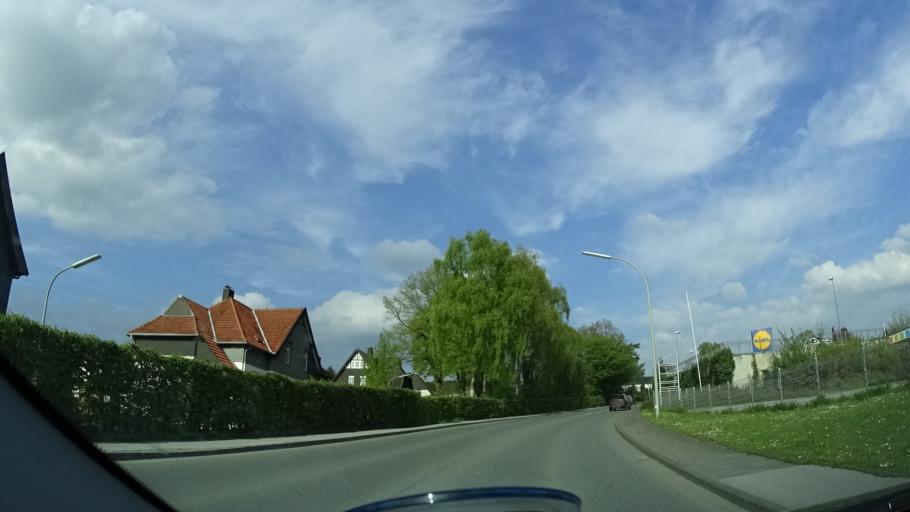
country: DE
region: North Rhine-Westphalia
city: Warstein
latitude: 51.4534
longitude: 8.3582
